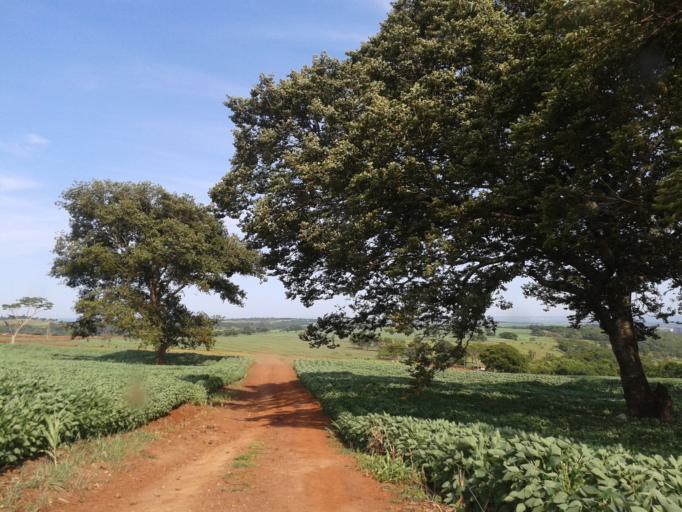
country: BR
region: Minas Gerais
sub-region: Centralina
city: Centralina
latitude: -18.7100
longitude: -49.2061
